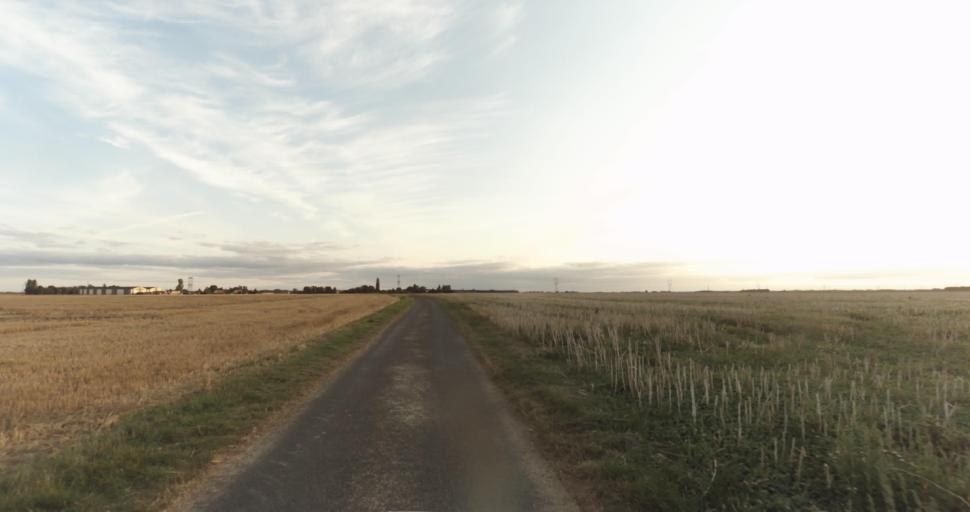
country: FR
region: Haute-Normandie
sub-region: Departement de l'Eure
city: La Madeleine-de-Nonancourt
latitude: 48.8590
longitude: 1.2202
